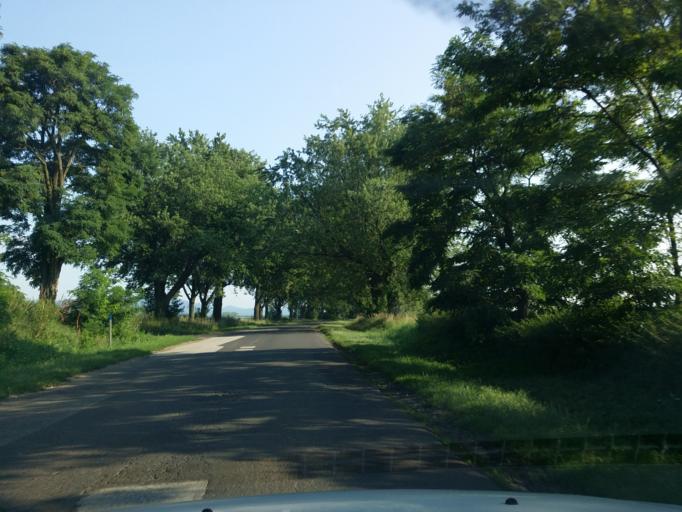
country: HU
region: Borsod-Abauj-Zemplen
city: Gonc
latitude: 48.4365
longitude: 21.2385
